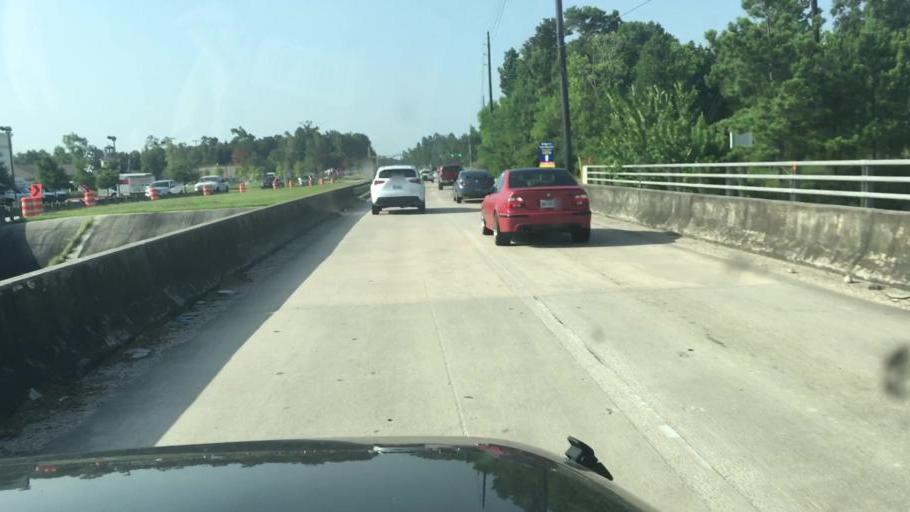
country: US
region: Texas
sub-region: Harris County
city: Atascocita
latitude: 29.9351
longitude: -95.1761
